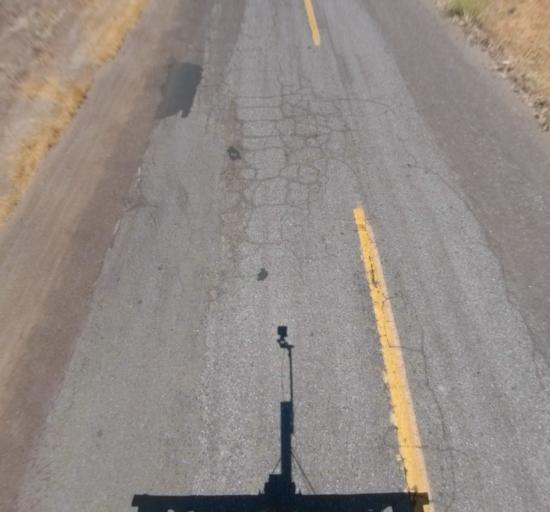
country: US
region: California
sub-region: Madera County
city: Chowchilla
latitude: 37.0198
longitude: -120.2925
